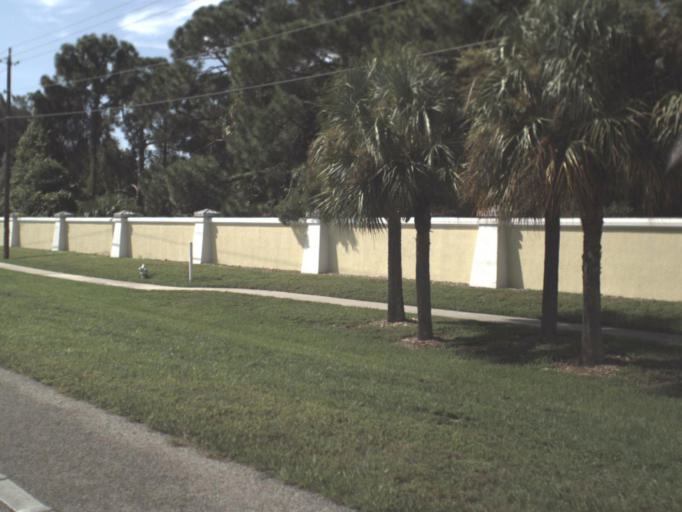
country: US
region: Florida
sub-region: Sarasota County
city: Osprey
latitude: 27.1933
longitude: -82.4894
